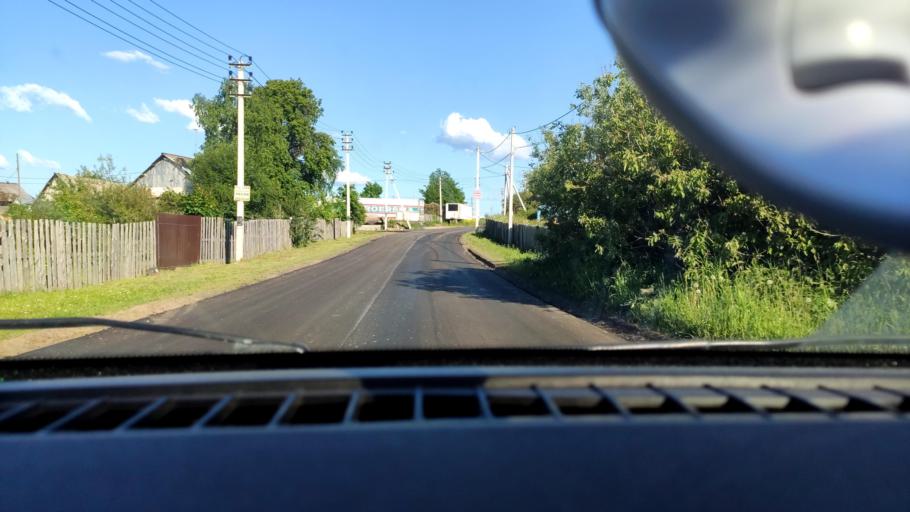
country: RU
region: Perm
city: Ferma
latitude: 57.9186
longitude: 56.3302
